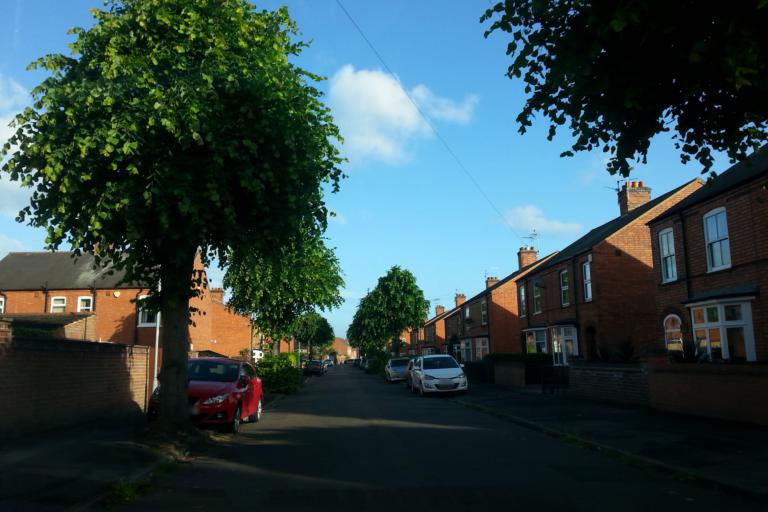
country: GB
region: England
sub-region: Nottinghamshire
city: Newark on Trent
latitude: 53.0708
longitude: -0.8117
